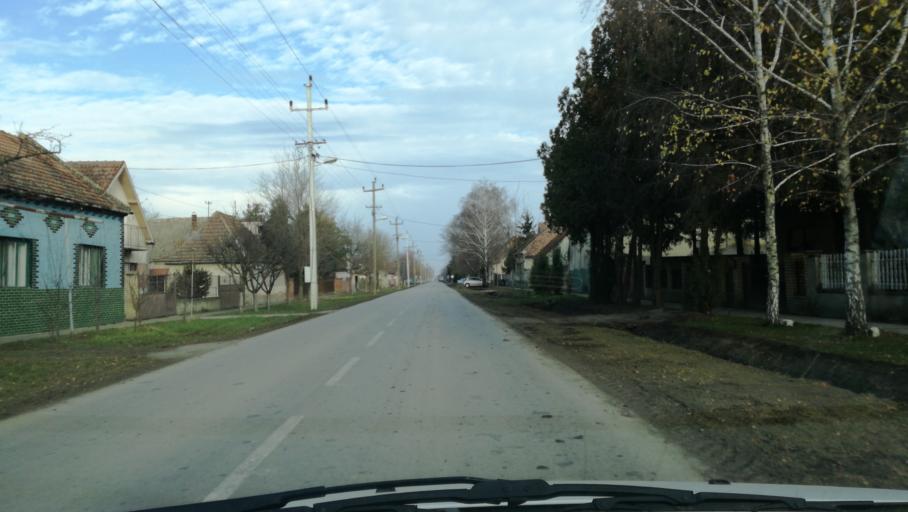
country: RS
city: Rusko Selo
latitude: 45.7523
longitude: 20.5668
